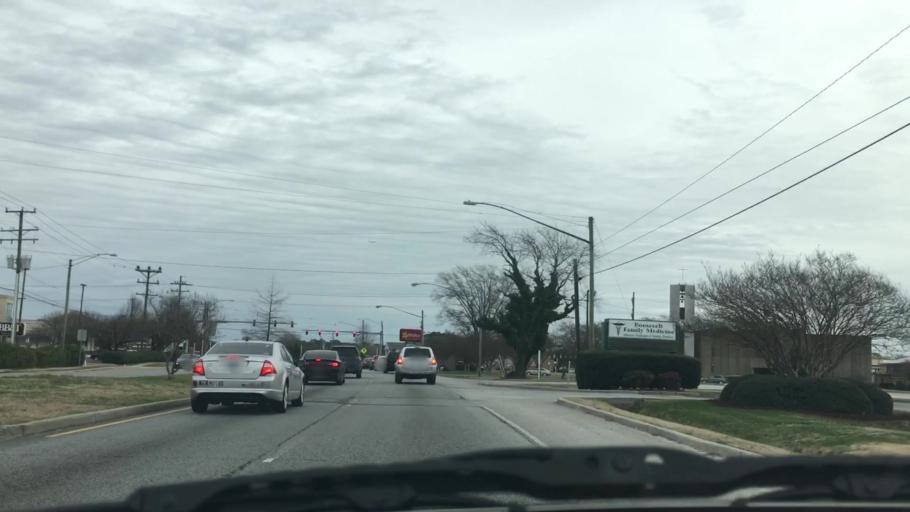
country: US
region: Virginia
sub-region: City of Norfolk
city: Norfolk
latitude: 36.9153
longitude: -76.2224
